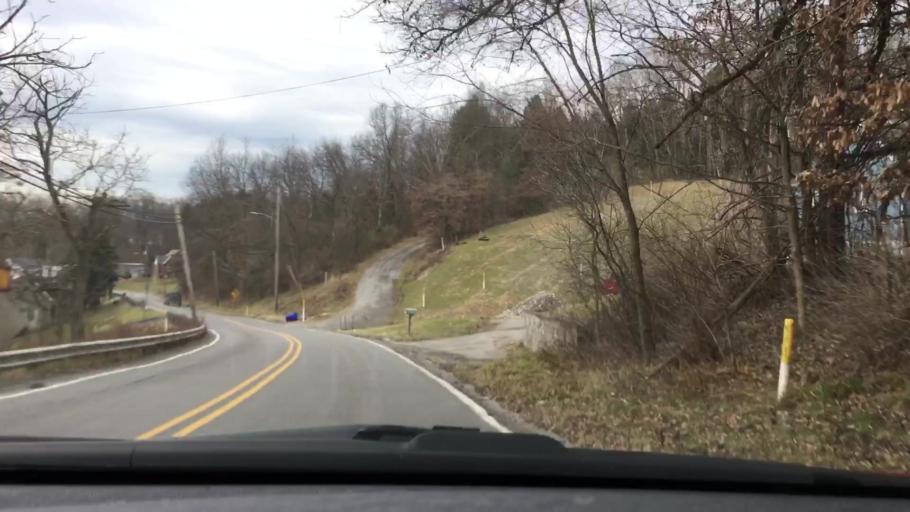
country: US
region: Pennsylvania
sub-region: Allegheny County
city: Sturgeon
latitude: 40.3905
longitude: -80.2024
